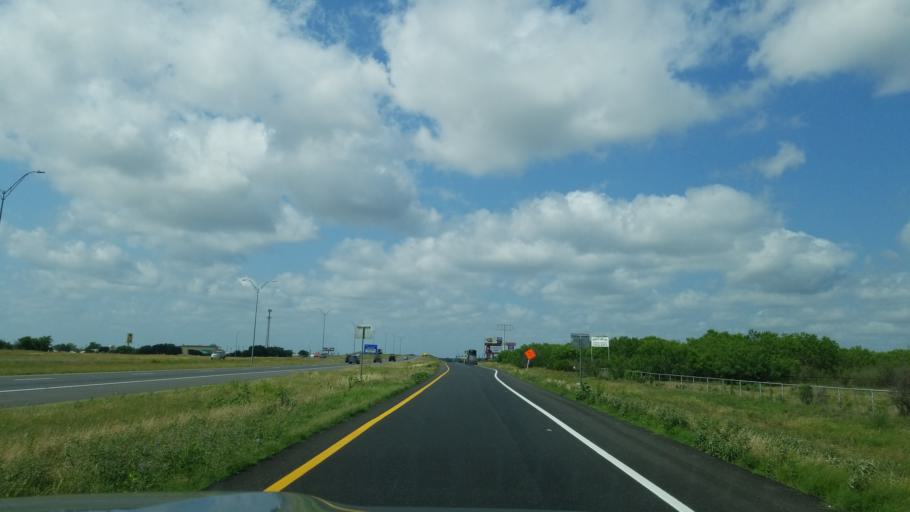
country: US
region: Texas
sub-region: Atascosa County
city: Lytle
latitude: 29.2338
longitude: -98.7835
